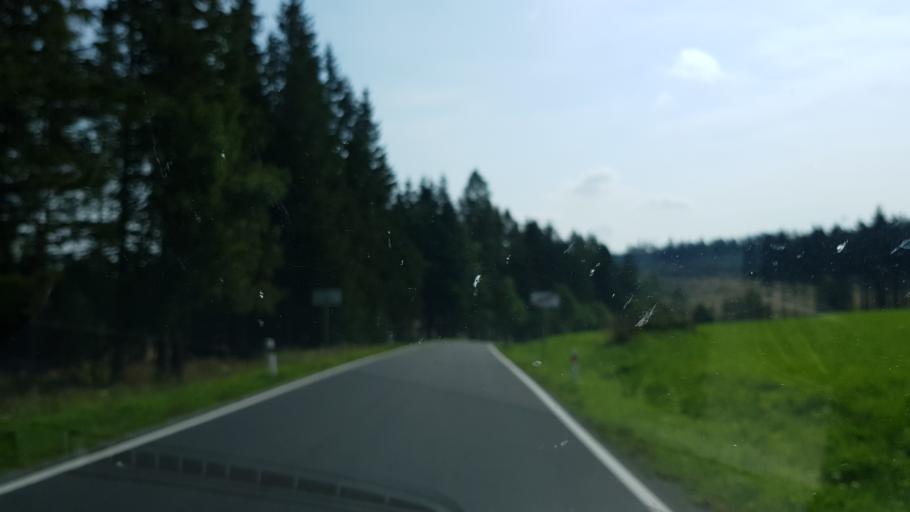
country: CZ
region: Olomoucky
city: Mikulovice
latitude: 50.2293
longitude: 17.3210
